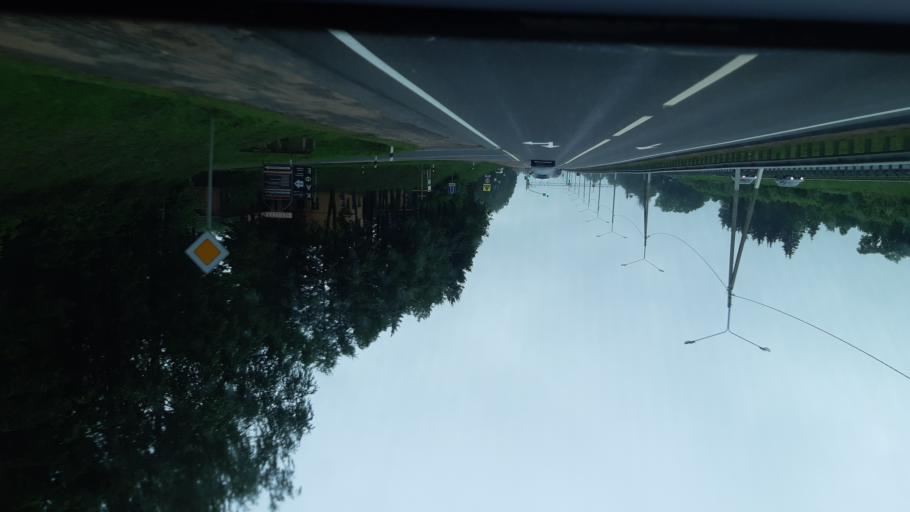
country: RU
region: Smolensk
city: Talashkino
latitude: 54.6794
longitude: 32.1420
